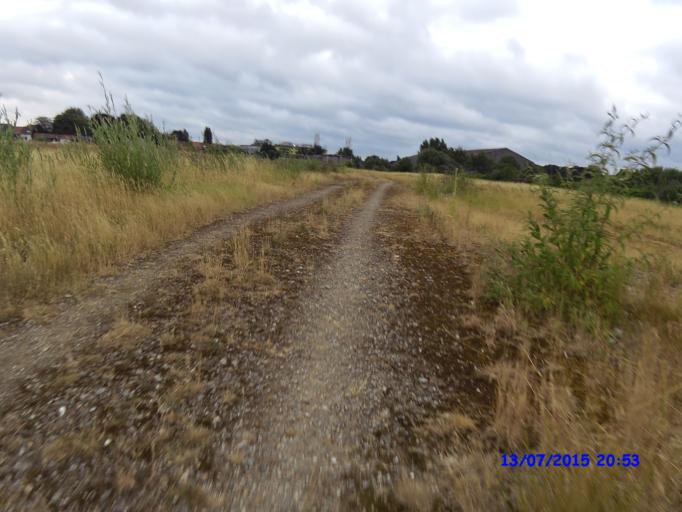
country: BE
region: Flanders
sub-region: Provincie Vlaams-Brabant
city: Vilvoorde
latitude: 50.9324
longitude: 4.4143
